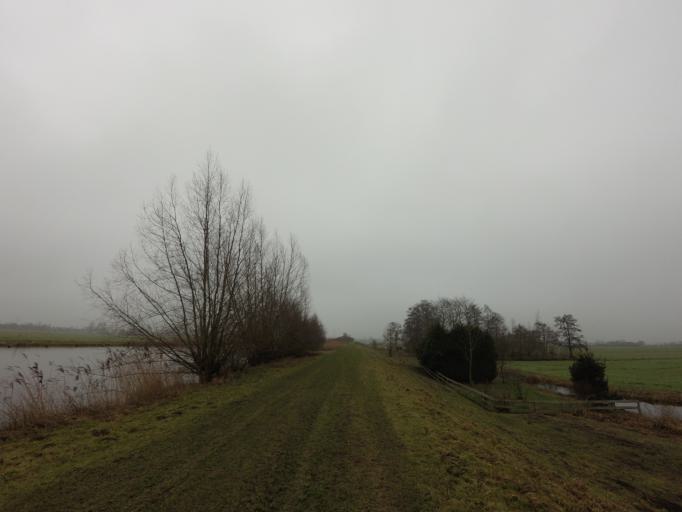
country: NL
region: South Holland
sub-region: Gemeente Vlist
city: Haastrecht
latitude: 52.0297
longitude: 4.7899
